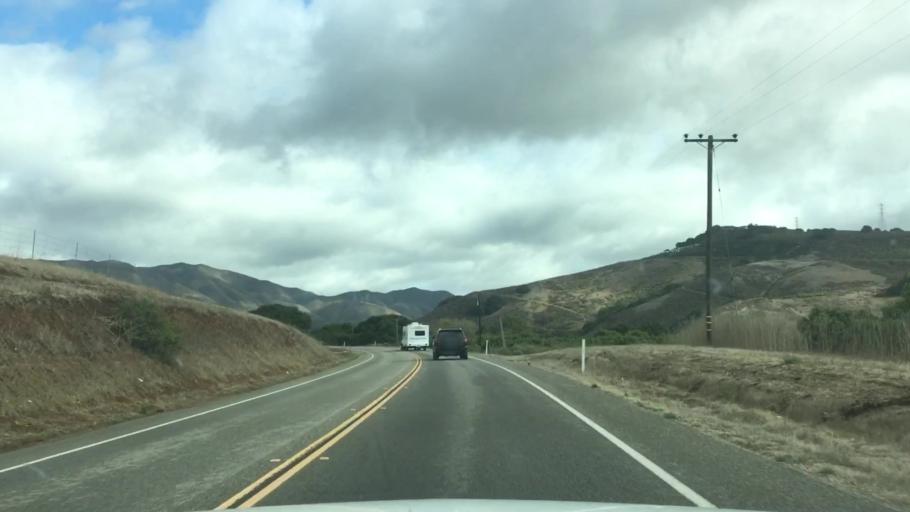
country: US
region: California
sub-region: San Luis Obispo County
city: Morro Bay
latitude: 35.4033
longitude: -120.8185
